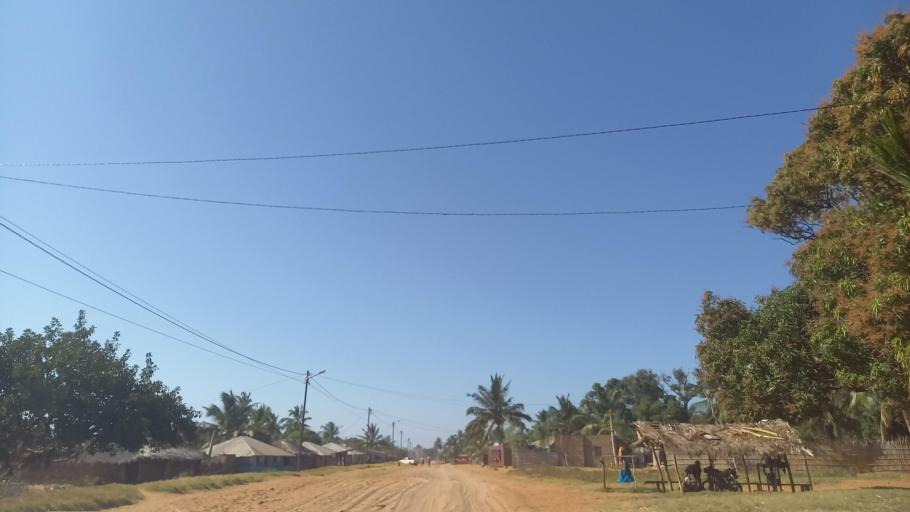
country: MZ
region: Cabo Delgado
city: Pemba
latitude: -13.1390
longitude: 40.5515
